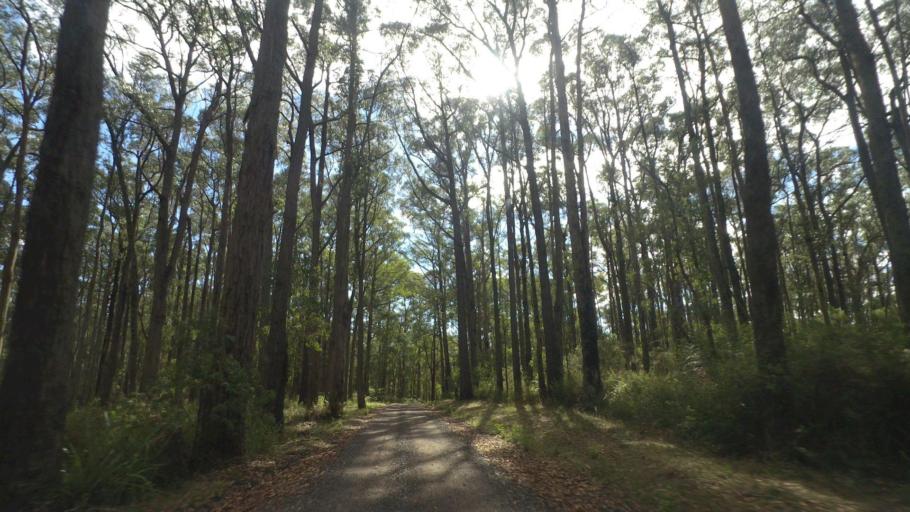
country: AU
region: Victoria
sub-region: Cardinia
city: Gembrook
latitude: -37.9133
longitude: 145.6006
